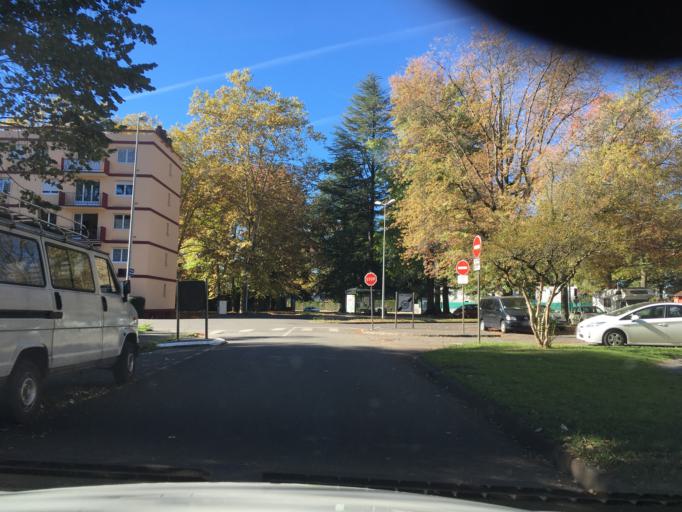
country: FR
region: Aquitaine
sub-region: Departement des Pyrenees-Atlantiques
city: Pau
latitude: 43.3093
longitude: -0.3688
